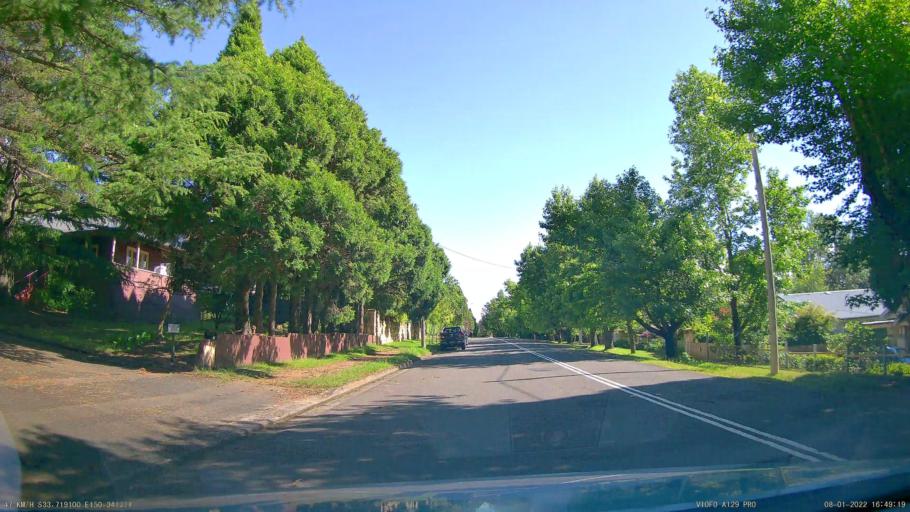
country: AU
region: New South Wales
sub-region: Blue Mountains Municipality
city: Leura
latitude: -33.7194
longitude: 150.3413
